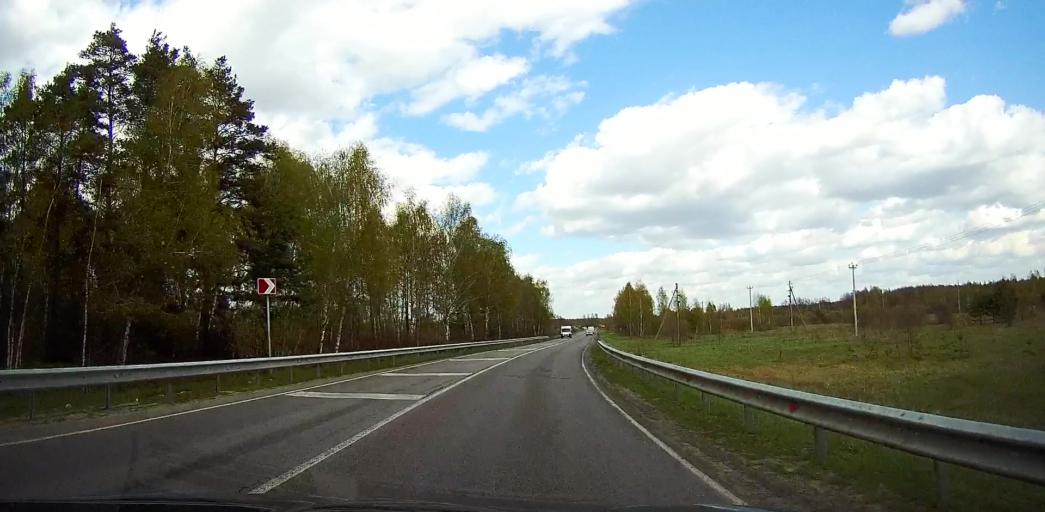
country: RU
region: Moskovskaya
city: Davydovo
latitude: 55.6294
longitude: 38.8631
